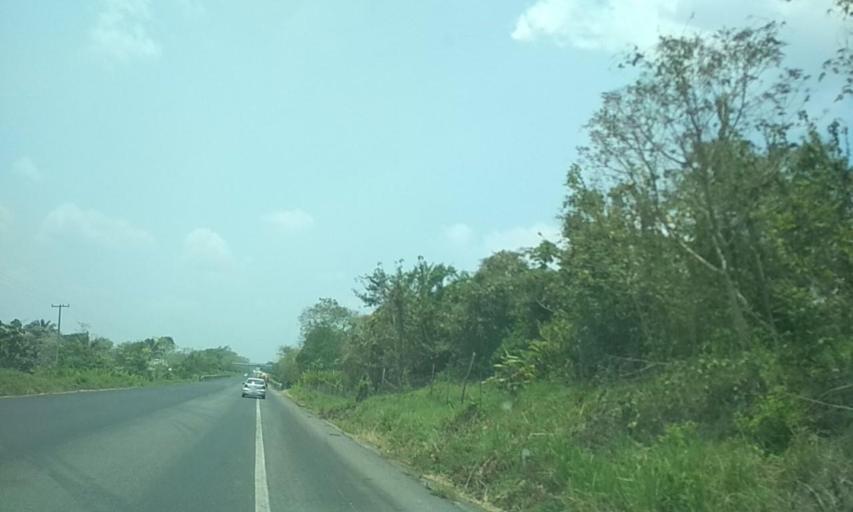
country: MX
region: Tabasco
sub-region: Huimanguillo
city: Francisco Rueda
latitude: 17.7024
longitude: -93.9291
